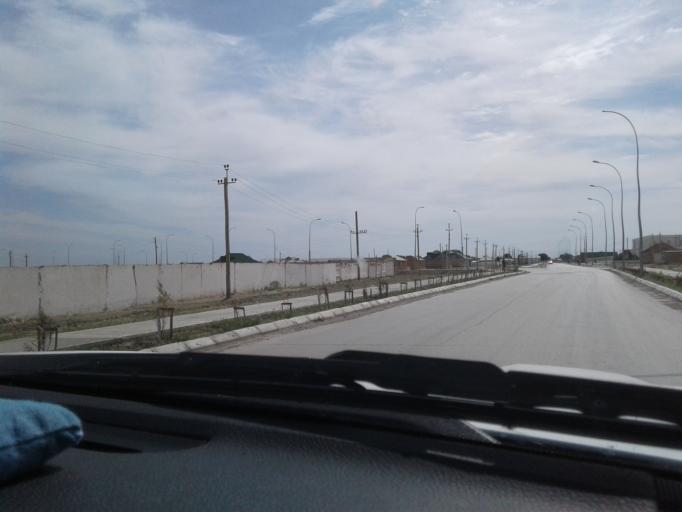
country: TM
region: Balkan
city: Gazanjyk
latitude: 39.2442
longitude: 55.4965
